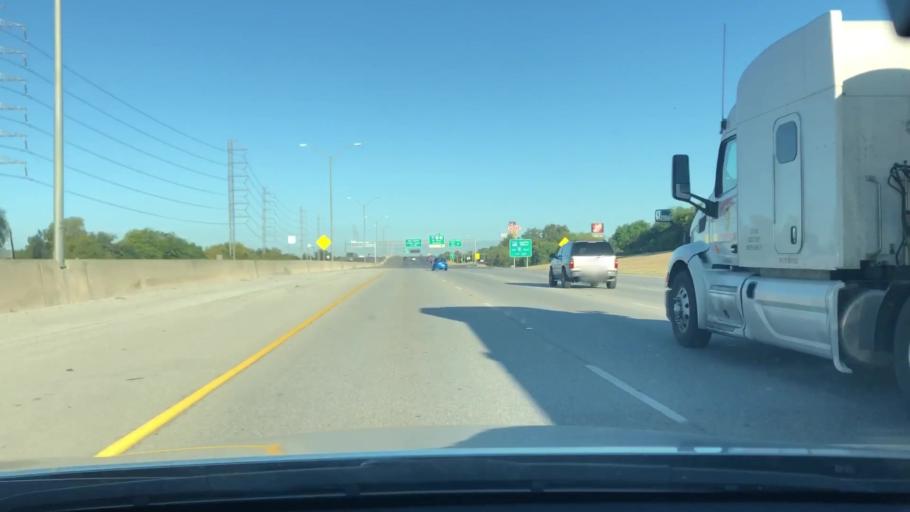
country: US
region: Texas
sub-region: Bexar County
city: San Antonio
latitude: 29.3805
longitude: -98.4652
